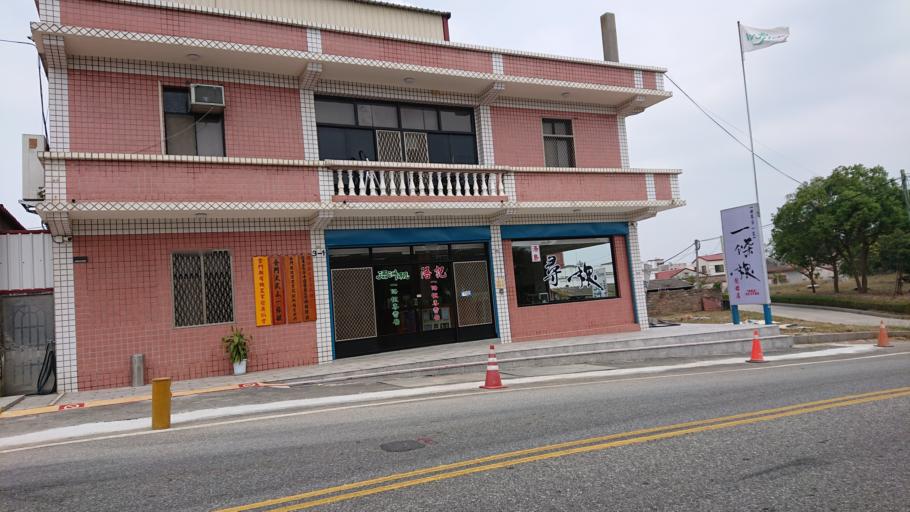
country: TW
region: Fukien
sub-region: Kinmen
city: Jincheng
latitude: 24.4587
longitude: 118.3627
